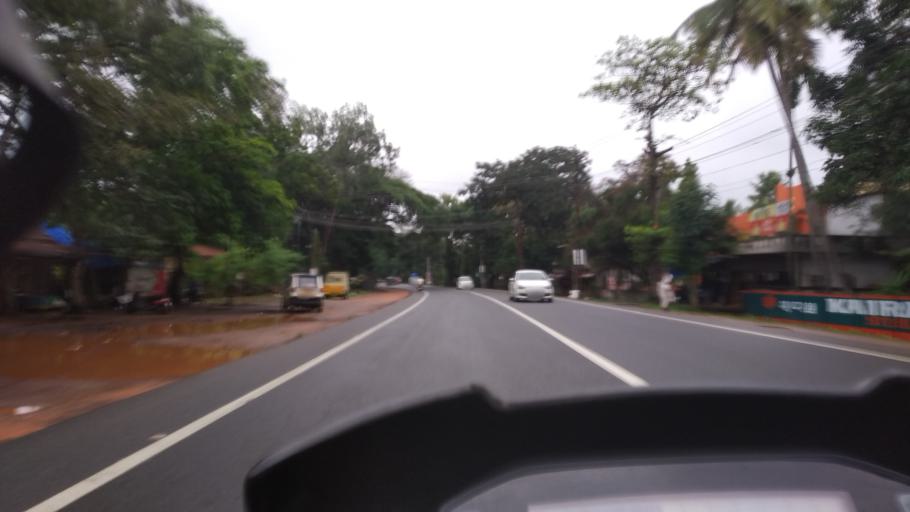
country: IN
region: Kerala
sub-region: Alappuzha
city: Mavelikara
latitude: 9.3079
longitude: 76.4317
